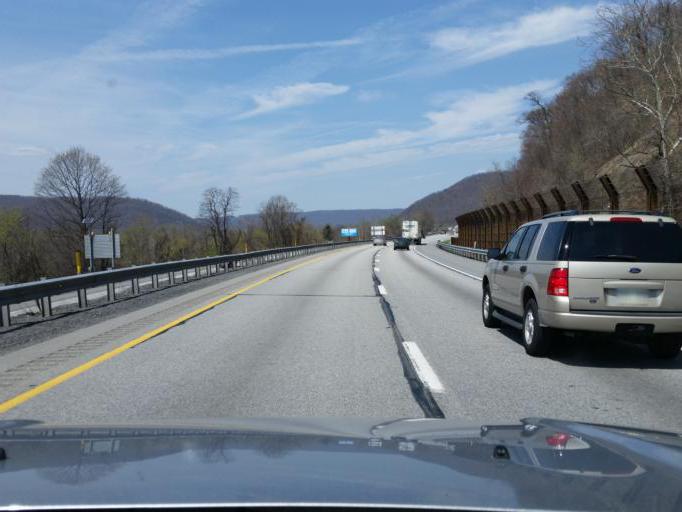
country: US
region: Pennsylvania
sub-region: Perry County
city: Marysville
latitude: 40.3334
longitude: -76.8998
